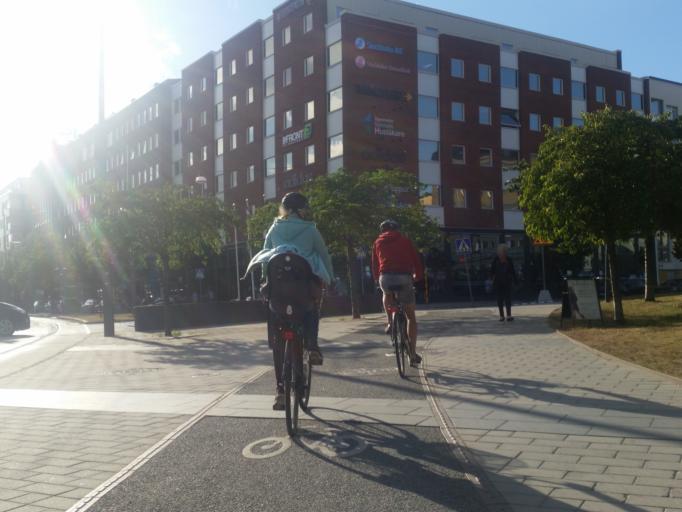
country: SE
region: Stockholm
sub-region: Stockholms Kommun
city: OEstermalm
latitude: 59.3043
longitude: 18.0949
